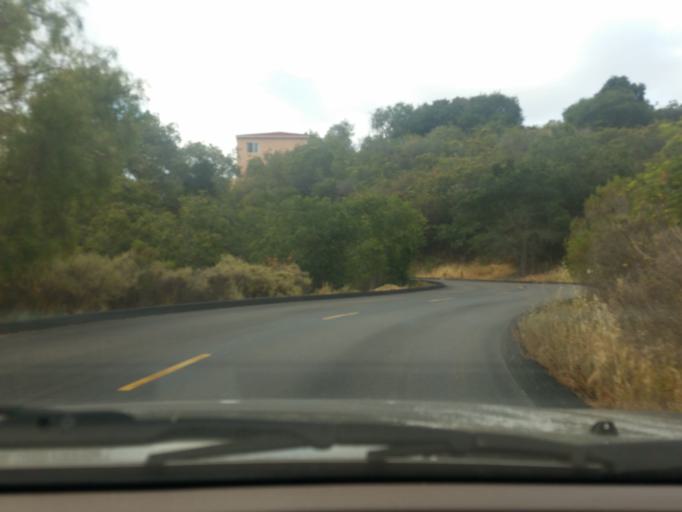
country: US
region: California
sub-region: San Luis Obispo County
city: Avila Beach
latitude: 35.1811
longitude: -120.7404
